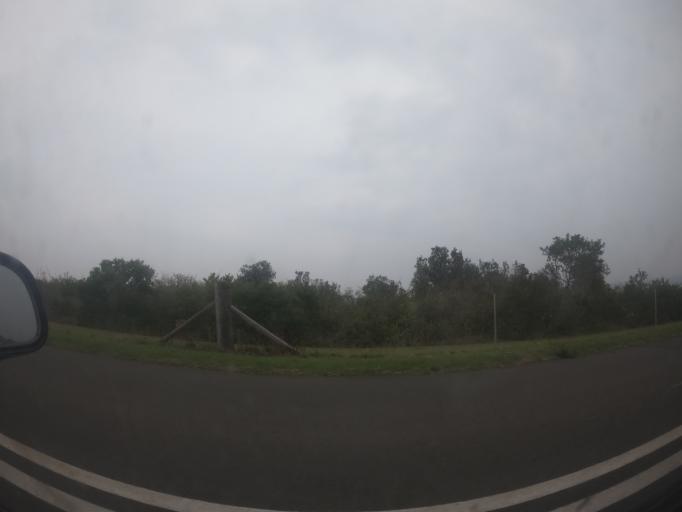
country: AU
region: New South Wales
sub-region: Shellharbour
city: Croom
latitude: -34.6104
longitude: 150.8589
